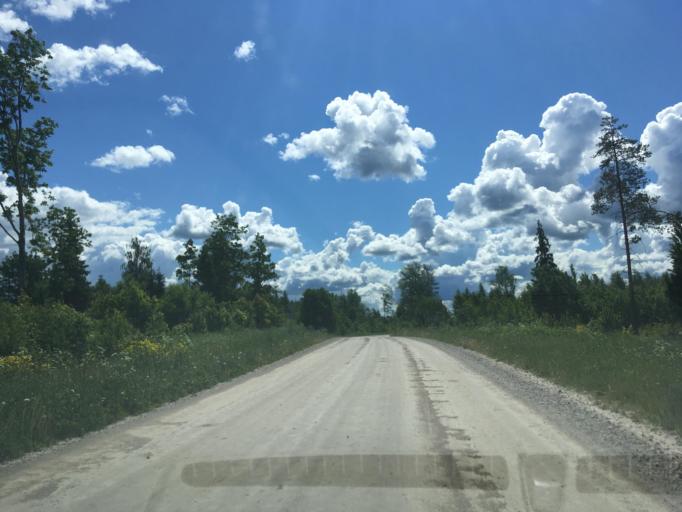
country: EE
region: Harju
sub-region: Nissi vald
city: Turba
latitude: 58.9325
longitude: 24.1515
